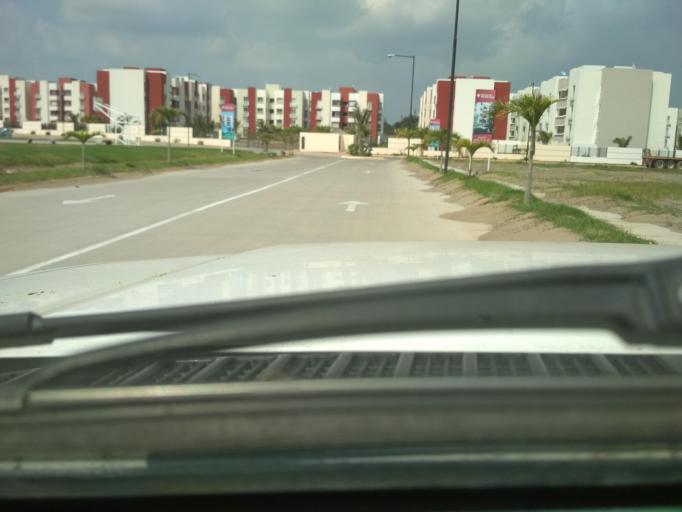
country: MX
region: Veracruz
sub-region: Veracruz
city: Lomas de Rio Medio Cuatro
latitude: 19.1797
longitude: -96.2087
